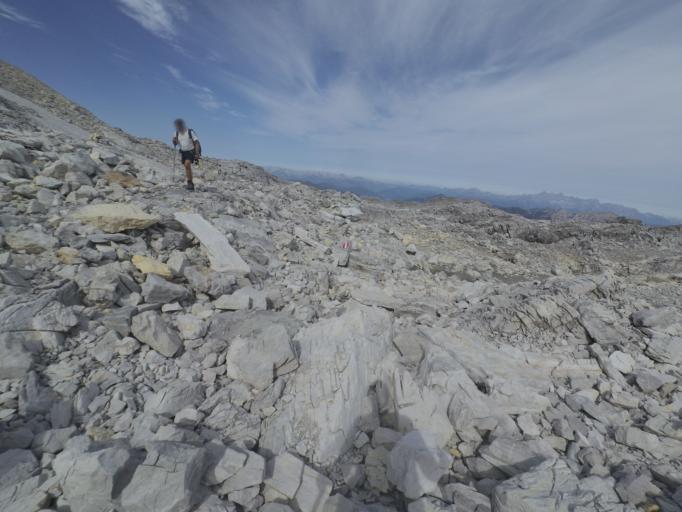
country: AT
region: Salzburg
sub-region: Politischer Bezirk Sankt Johann im Pongau
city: Kleinarl
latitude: 47.2084
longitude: 13.3912
